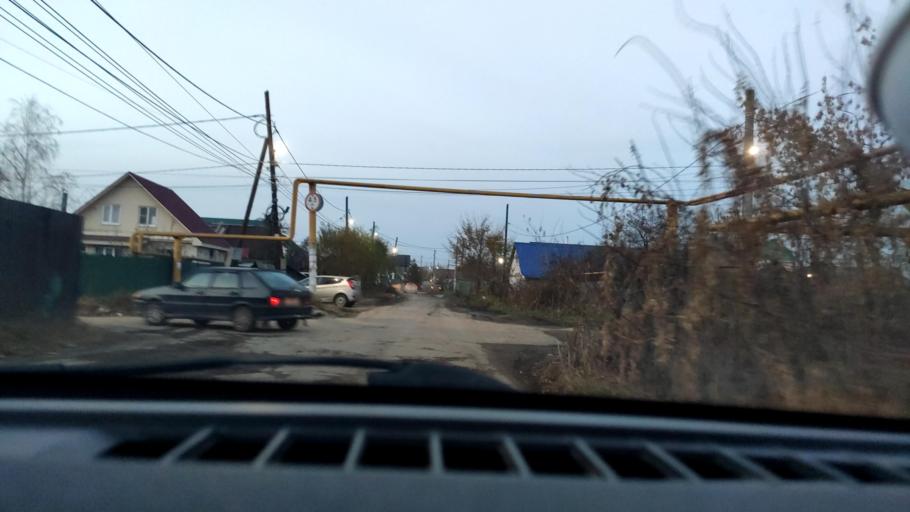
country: RU
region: Samara
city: Samara
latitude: 53.1380
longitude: 50.0959
